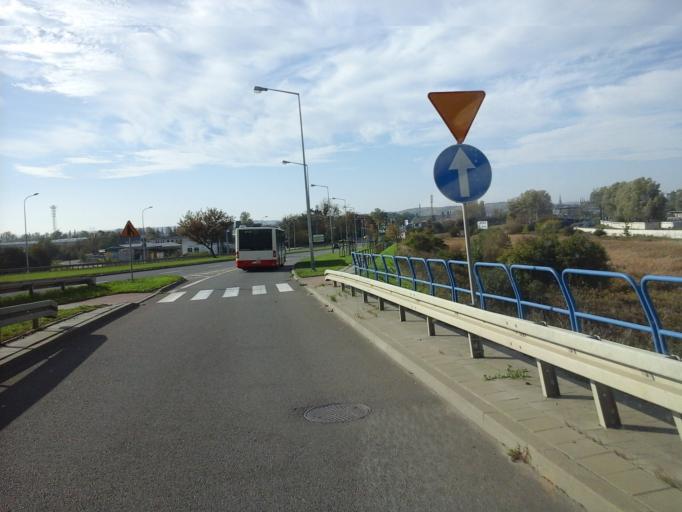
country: PL
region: Pomeranian Voivodeship
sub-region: Gdansk
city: Gdansk
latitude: 54.3498
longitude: 18.6953
